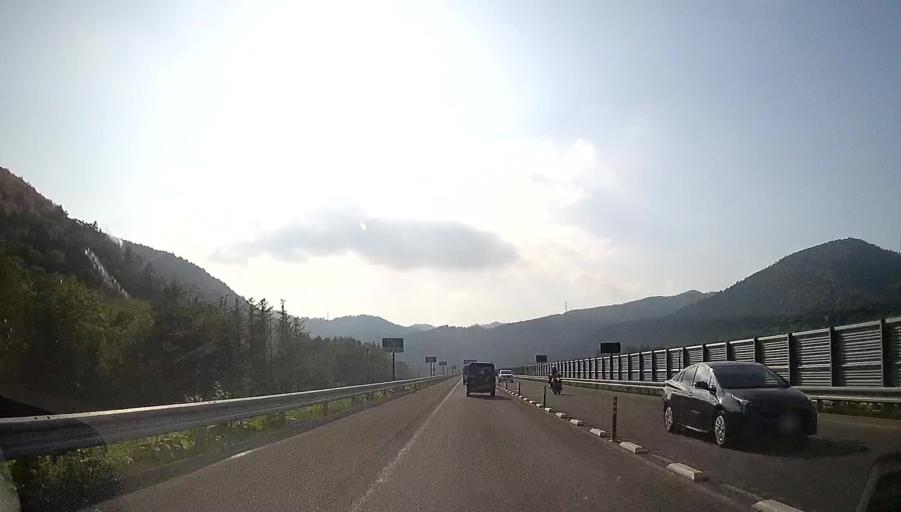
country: JP
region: Hokkaido
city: Shimo-furano
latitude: 43.0621
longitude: 142.5522
